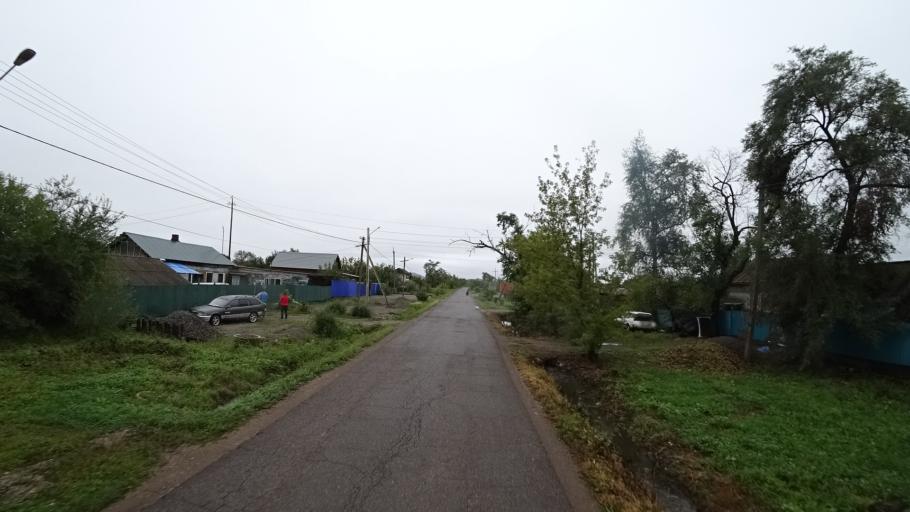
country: RU
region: Primorskiy
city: Monastyrishche
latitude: 44.2023
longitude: 132.4607
